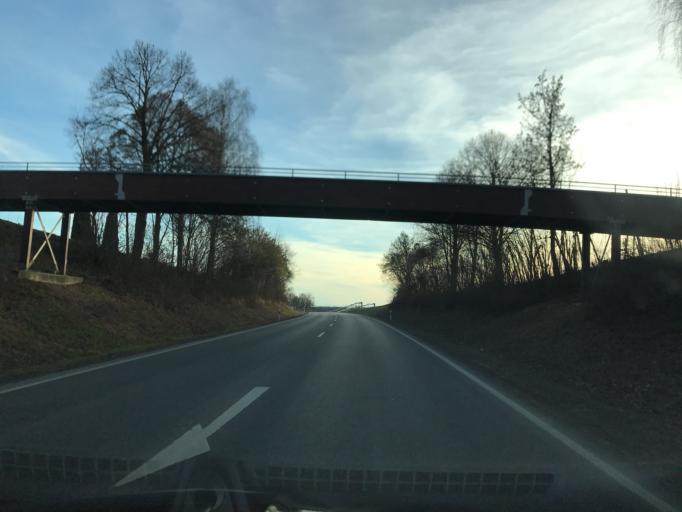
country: DE
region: Baden-Wuerttemberg
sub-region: Tuebingen Region
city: Meckenbeuren
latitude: 47.7248
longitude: 9.5858
